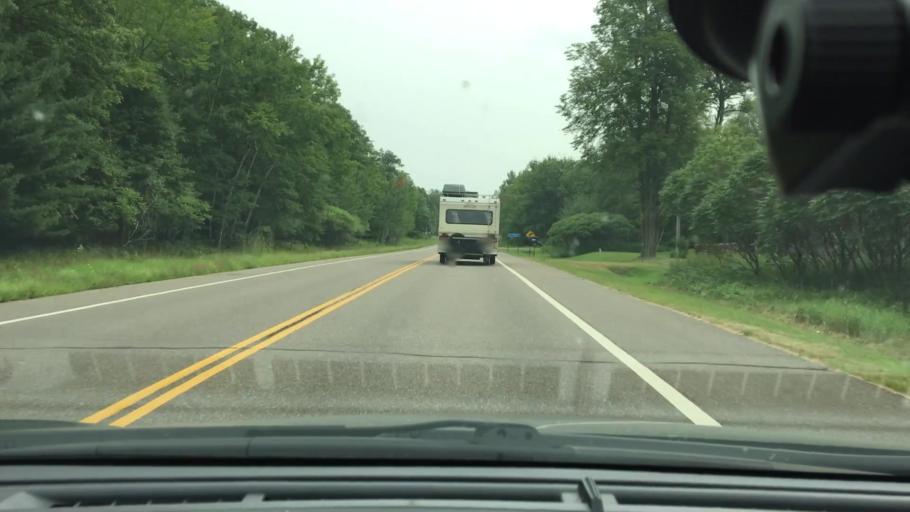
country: US
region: Minnesota
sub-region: Crow Wing County
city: Crosby
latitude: 46.4073
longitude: -93.8137
